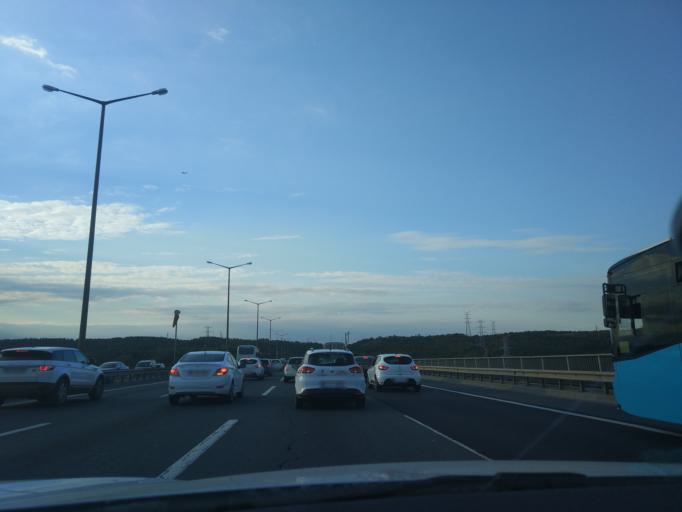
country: TR
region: Istanbul
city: Umraniye
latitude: 41.0733
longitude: 29.1033
